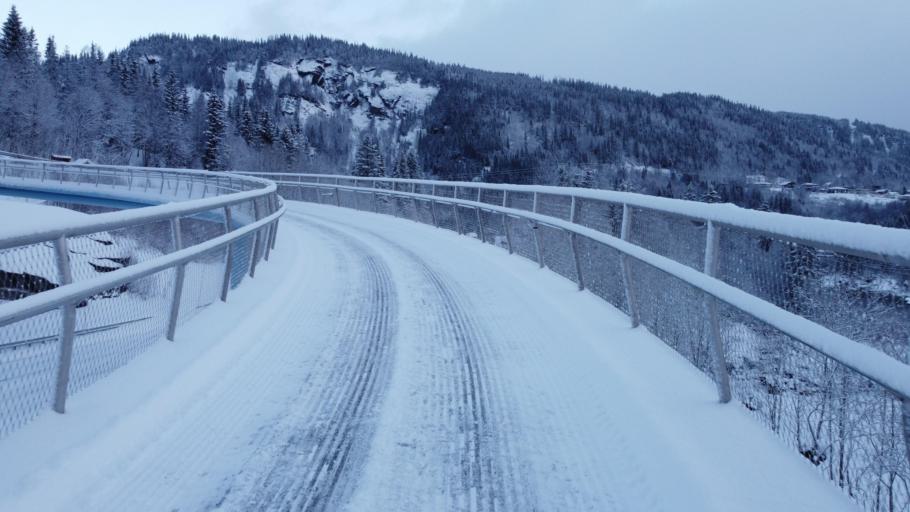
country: NO
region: Nordland
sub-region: Rana
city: Mo i Rana
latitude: 66.3294
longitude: 14.1619
